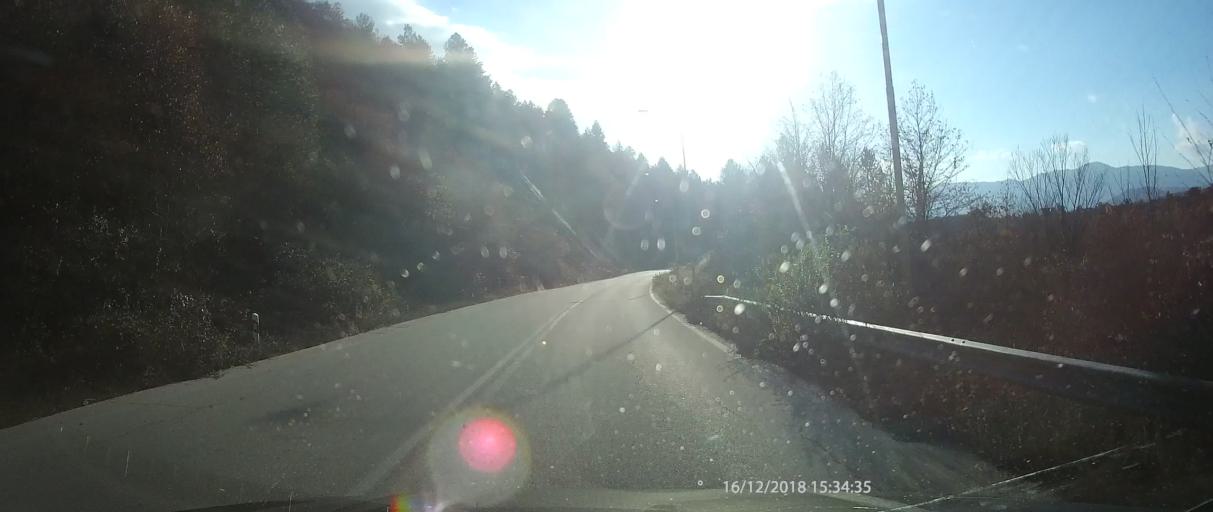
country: GR
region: Epirus
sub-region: Nomos Ioanninon
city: Konitsa
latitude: 40.0596
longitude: 20.7406
